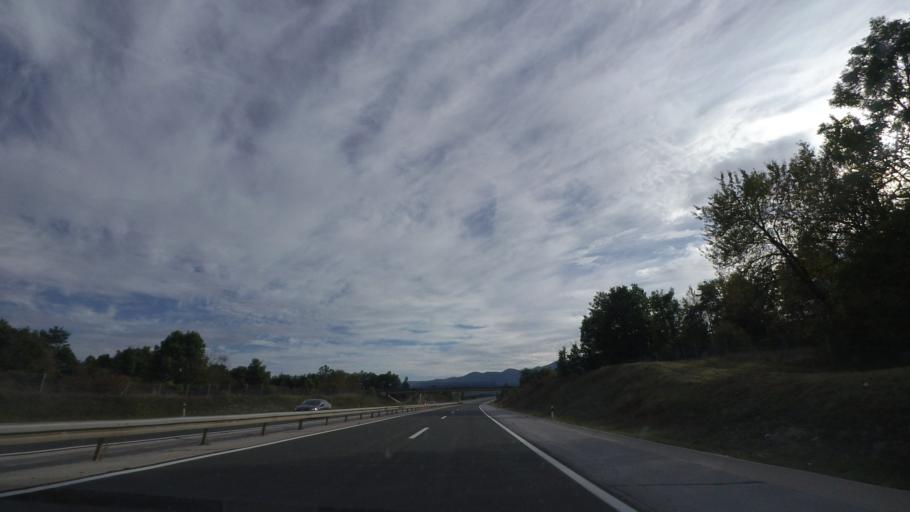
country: HR
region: Zadarska
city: Obrovac
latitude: 44.4096
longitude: 15.6387
